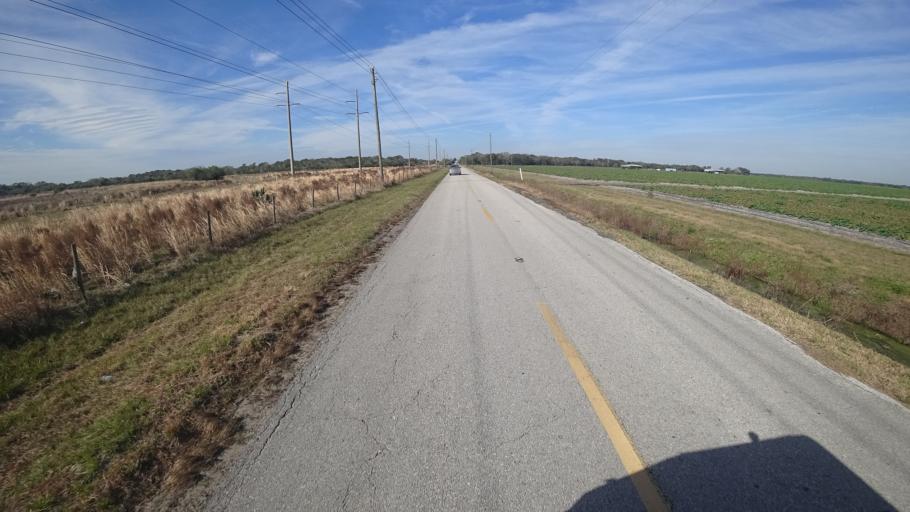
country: US
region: Florida
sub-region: Manatee County
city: Ellenton
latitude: 27.6232
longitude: -82.5005
